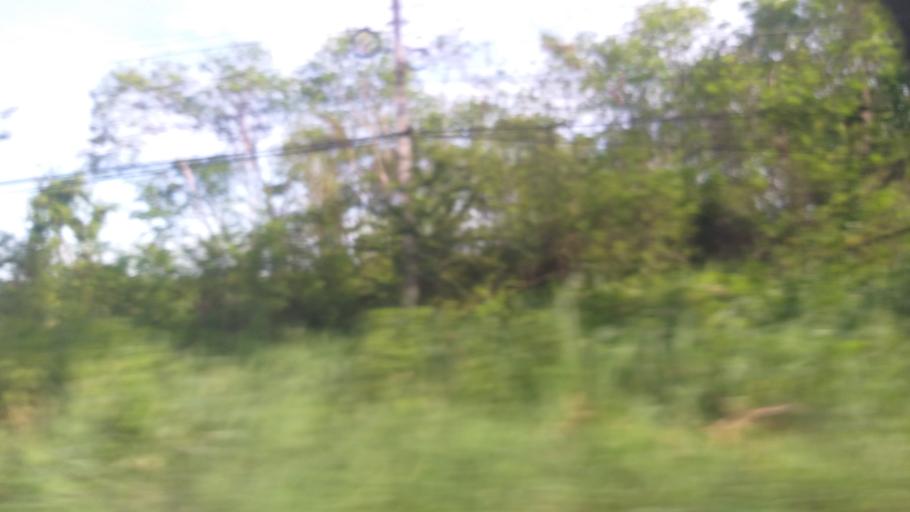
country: TH
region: Chaiyaphum
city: Ban Thaen
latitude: 16.4014
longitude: 102.3398
